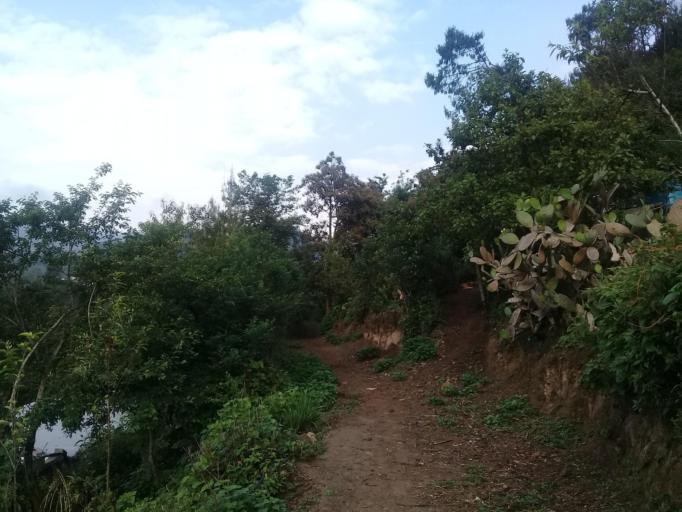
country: MX
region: Veracruz
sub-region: Mariano Escobedo
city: San Isidro el Berro
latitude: 18.9505
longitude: -97.2006
